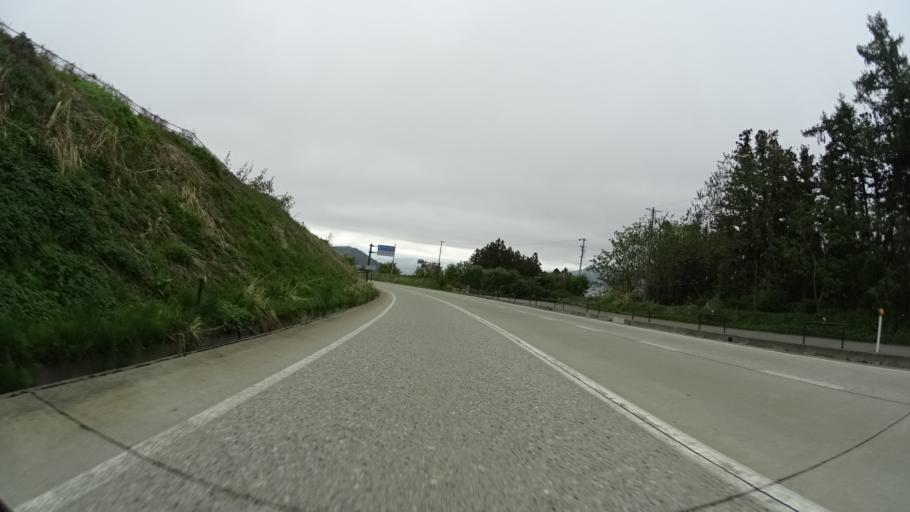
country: JP
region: Nagano
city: Nakano
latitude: 36.7335
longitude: 138.4198
